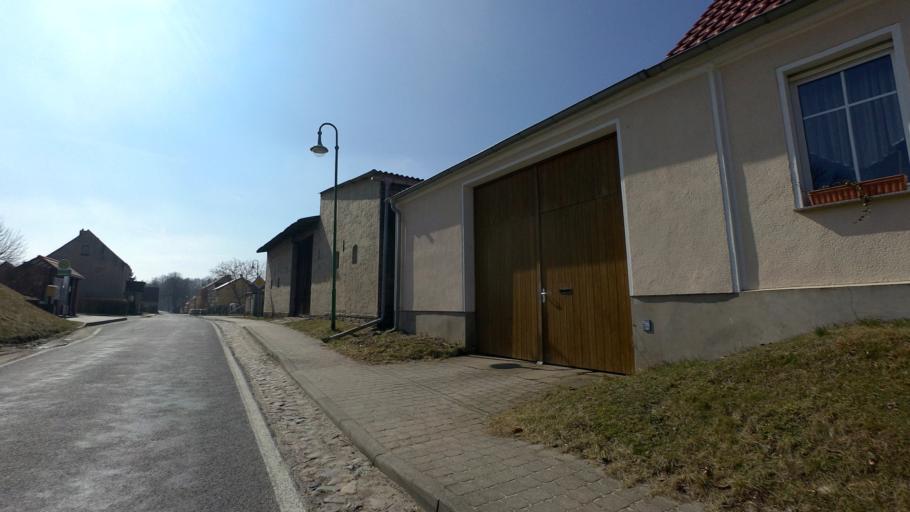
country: DE
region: Brandenburg
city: Wiesenburg
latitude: 52.0370
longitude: 12.5185
